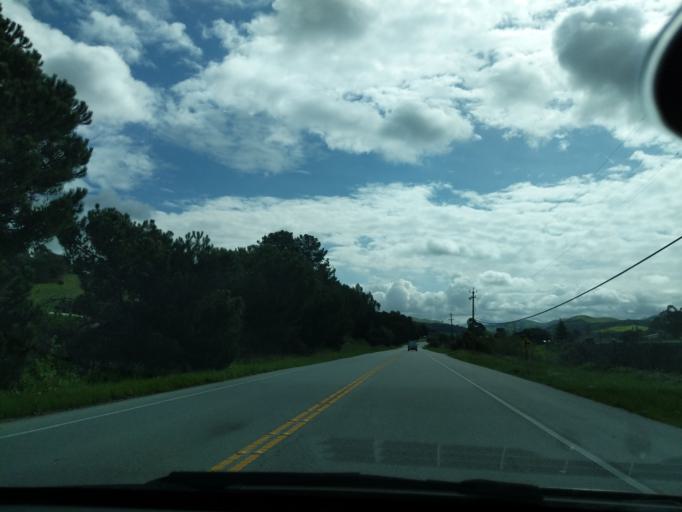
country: US
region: California
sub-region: San Benito County
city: Aromas
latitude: 36.8584
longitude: -121.6480
